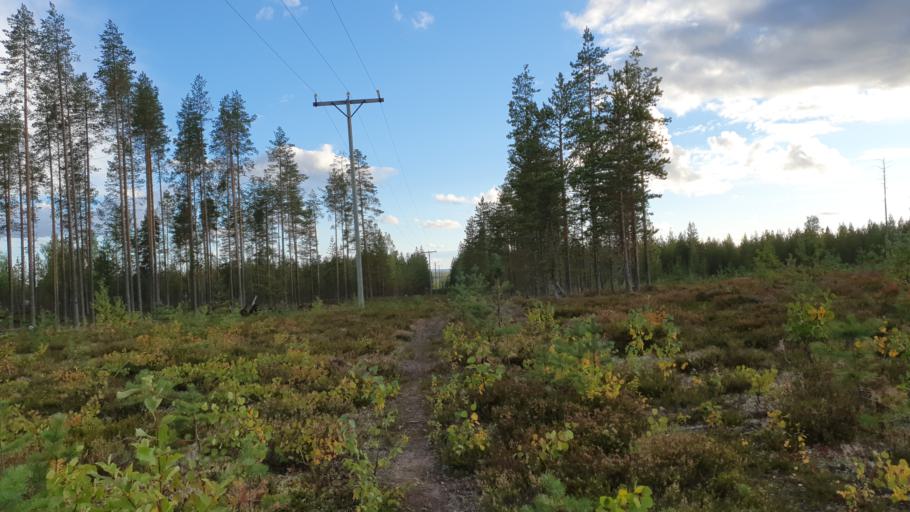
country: FI
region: Kainuu
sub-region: Kehys-Kainuu
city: Kuhmo
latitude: 64.1992
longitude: 29.1593
